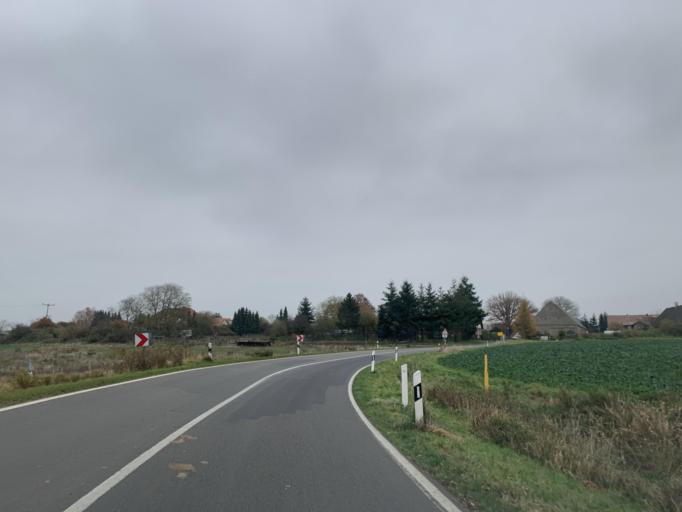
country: DE
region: Mecklenburg-Vorpommern
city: Blankensee
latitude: 53.4162
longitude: 13.2538
